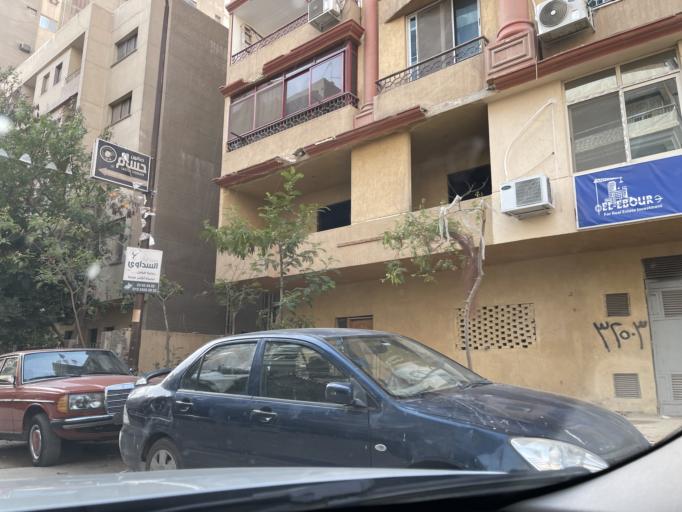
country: EG
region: Muhafazat al Qahirah
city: Cairo
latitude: 30.0684
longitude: 31.3517
